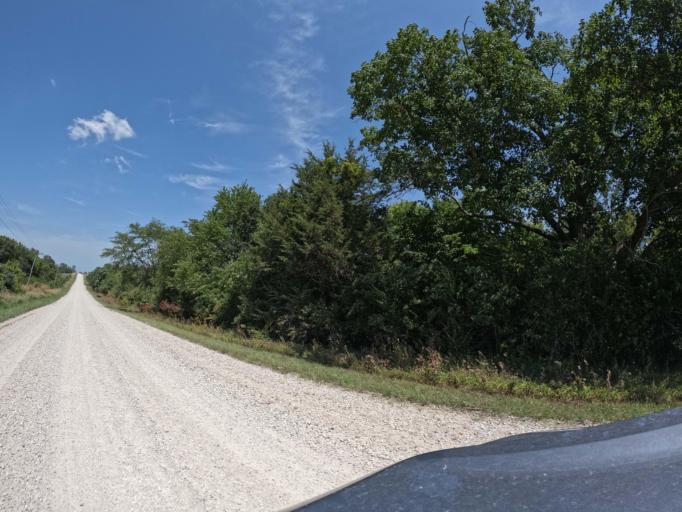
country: US
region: Iowa
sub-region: Henry County
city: Mount Pleasant
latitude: 40.9290
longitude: -91.6461
